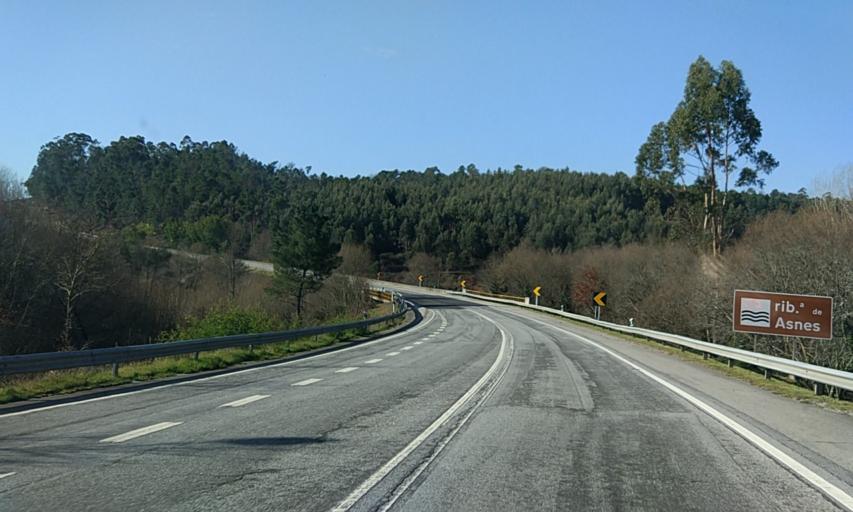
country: PT
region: Viseu
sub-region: Viseu
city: Abraveses
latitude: 40.6676
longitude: -7.9988
